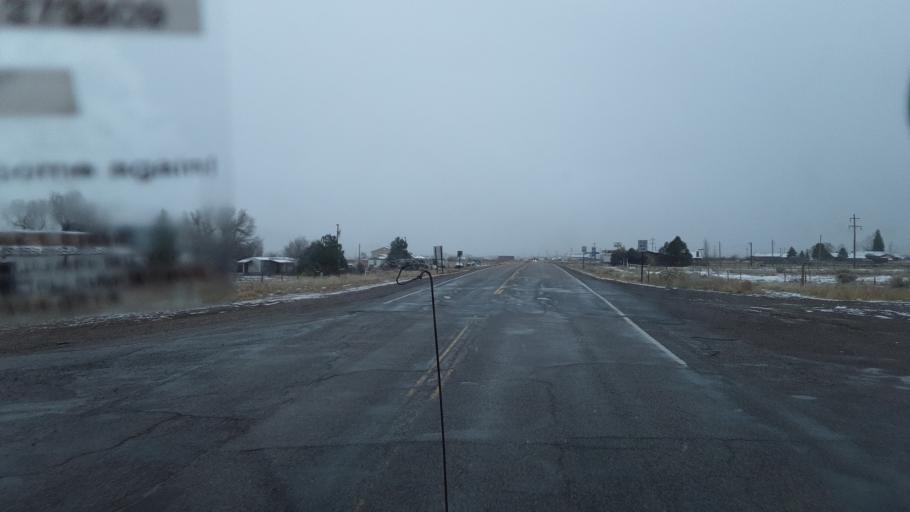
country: US
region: New Mexico
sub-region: Rio Arriba County
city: Tierra Amarilla
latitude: 36.7011
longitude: -106.5581
